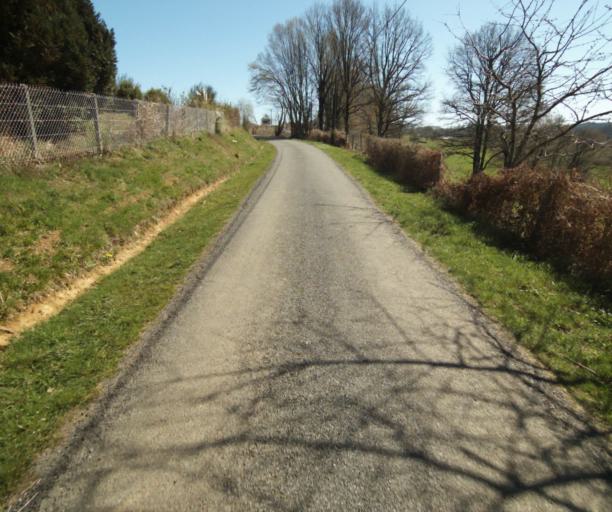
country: FR
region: Limousin
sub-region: Departement de la Correze
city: Uzerche
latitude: 45.4042
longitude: 1.6225
